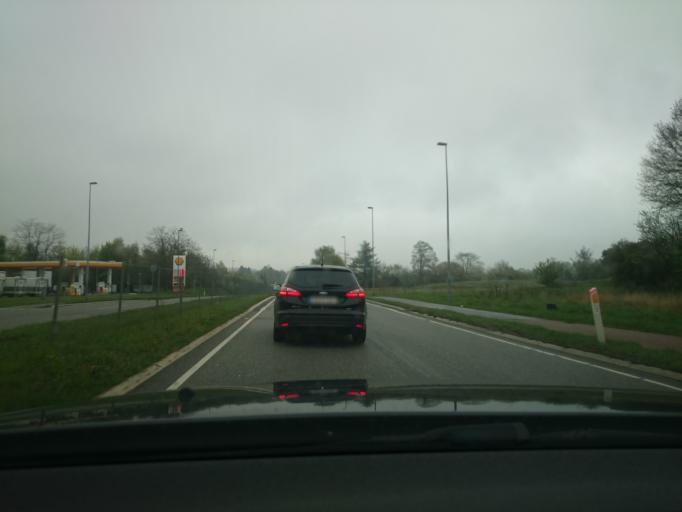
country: DK
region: Capital Region
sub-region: Ballerup Kommune
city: Ballerup
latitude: 55.7506
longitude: 12.4028
